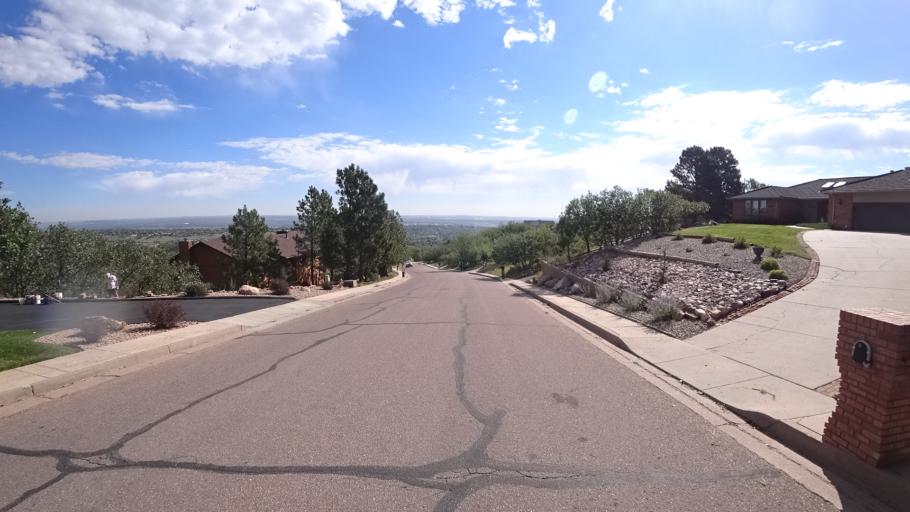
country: US
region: Colorado
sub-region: El Paso County
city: Fort Carson
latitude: 38.7655
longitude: -104.8242
